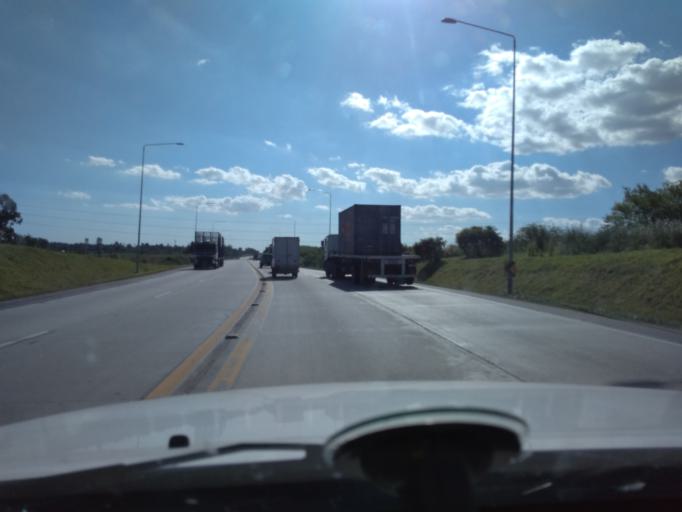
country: UY
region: Canelones
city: La Paz
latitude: -34.7797
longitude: -56.2353
